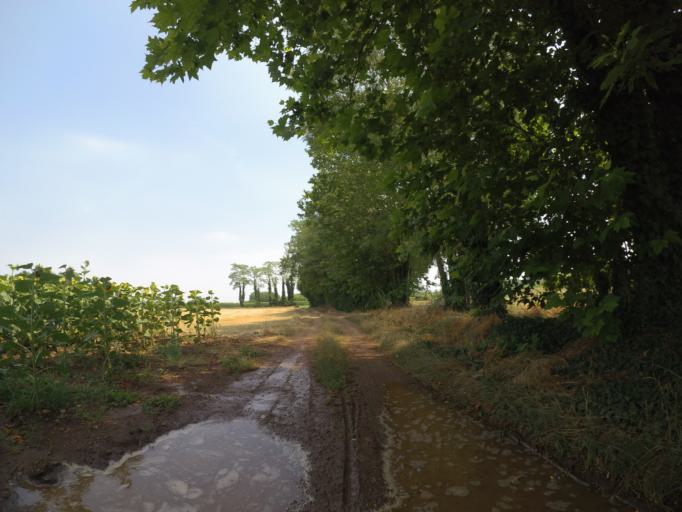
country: IT
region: Friuli Venezia Giulia
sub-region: Provincia di Udine
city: Bertiolo
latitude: 45.9553
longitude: 13.0693
